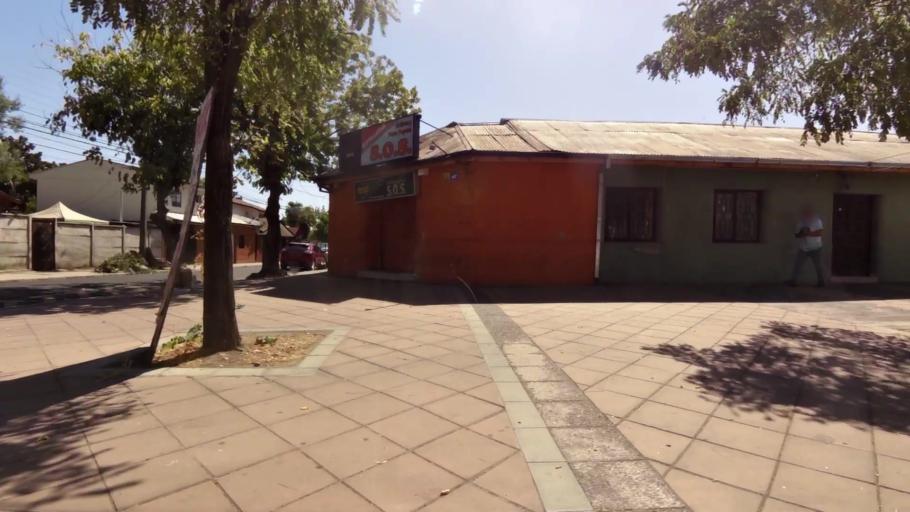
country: CL
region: Maule
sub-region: Provincia de Talca
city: Talca
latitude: -35.4322
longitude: -71.6588
